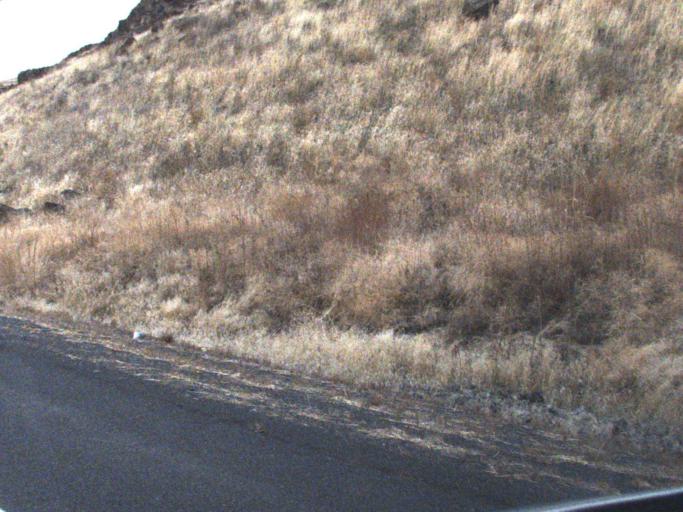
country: US
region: Washington
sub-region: Adams County
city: Ritzville
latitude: 46.7557
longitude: -118.1766
